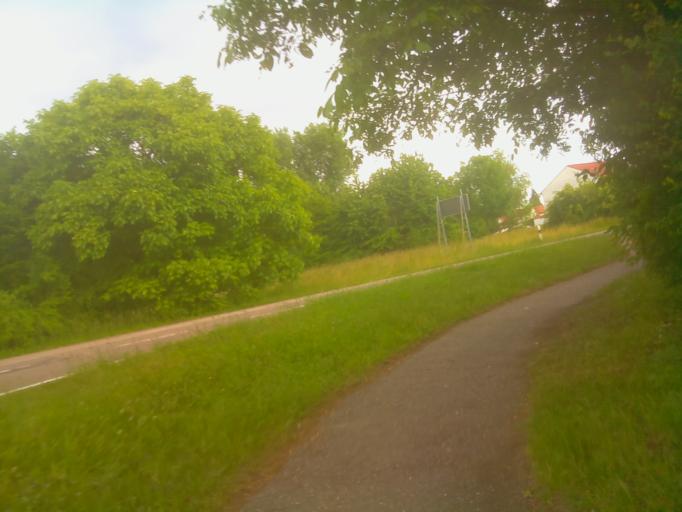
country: DE
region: Rheinland-Pfalz
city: Frankenthal
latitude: 49.5352
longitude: 8.3792
